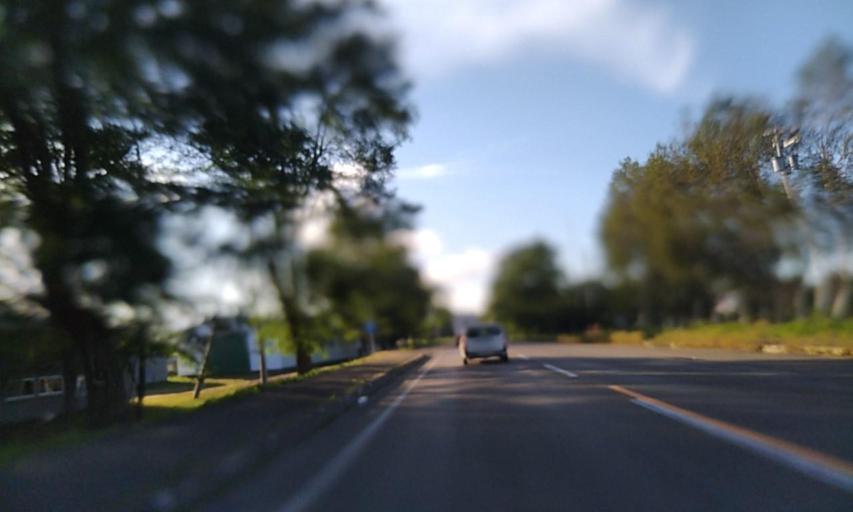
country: JP
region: Hokkaido
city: Obihiro
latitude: 42.9378
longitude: 142.9606
